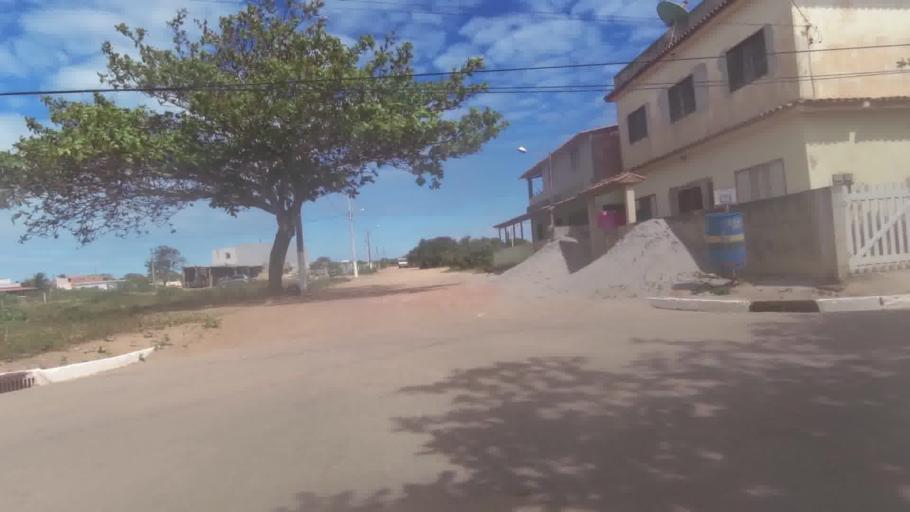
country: BR
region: Espirito Santo
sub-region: Marataizes
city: Marataizes
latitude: -21.1890
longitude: -40.9309
